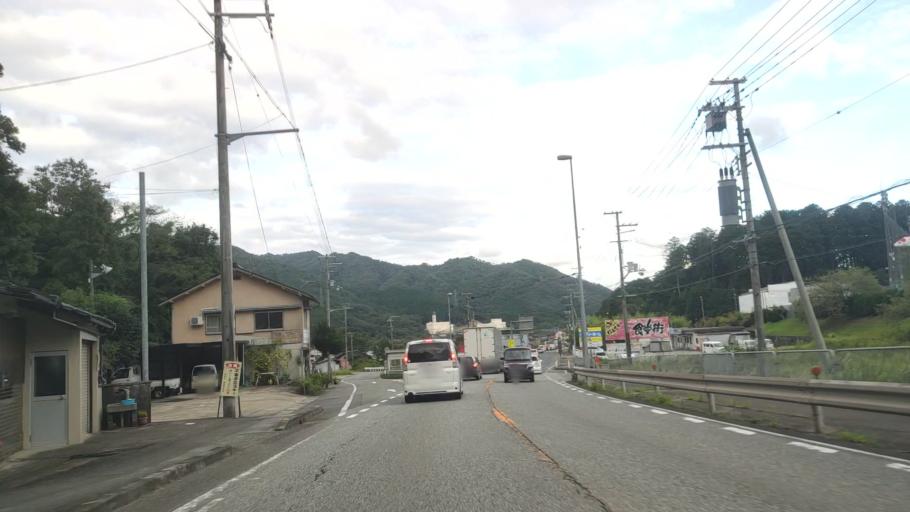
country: JP
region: Hyogo
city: Toyooka
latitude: 35.3674
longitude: 134.8085
